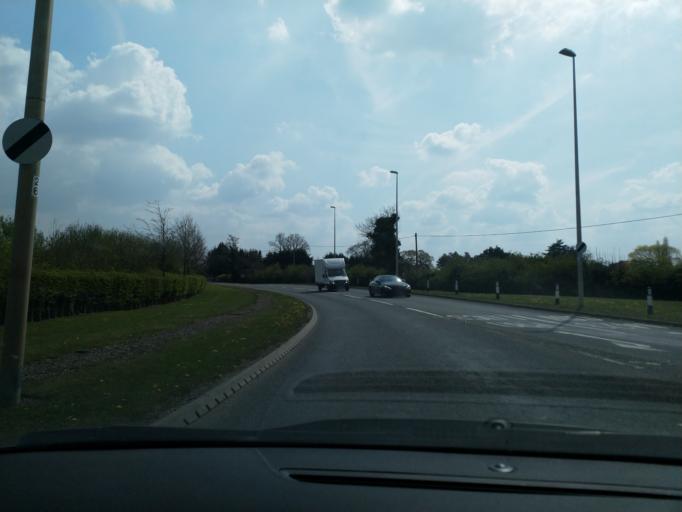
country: GB
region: England
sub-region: Warwickshire
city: Ryton on Dunsmore
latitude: 52.3660
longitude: -1.4472
